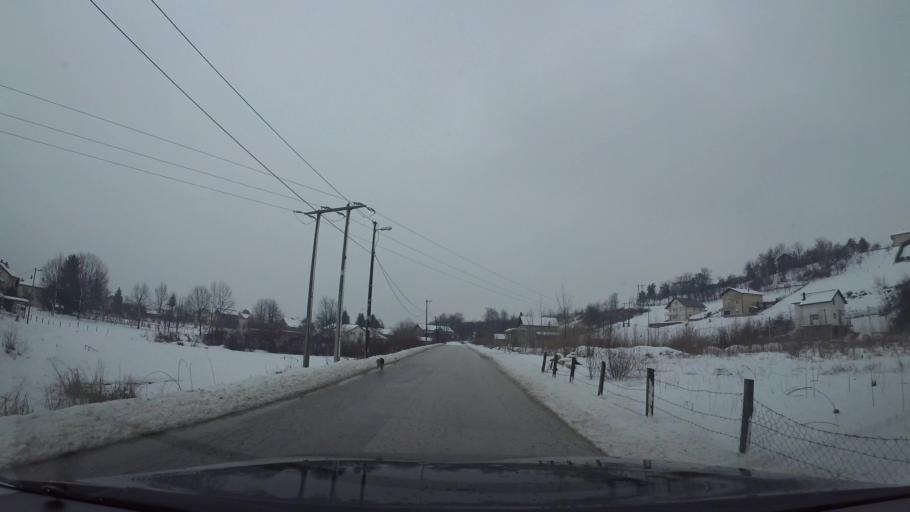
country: BA
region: Federation of Bosnia and Herzegovina
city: Hadzici
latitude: 43.8523
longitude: 18.2760
